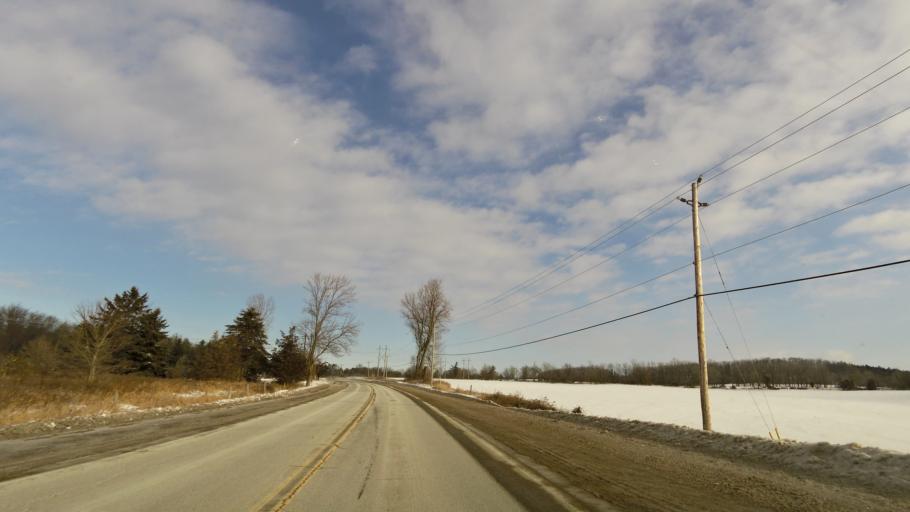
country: CA
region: Ontario
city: Quinte West
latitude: 44.0949
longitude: -77.7693
